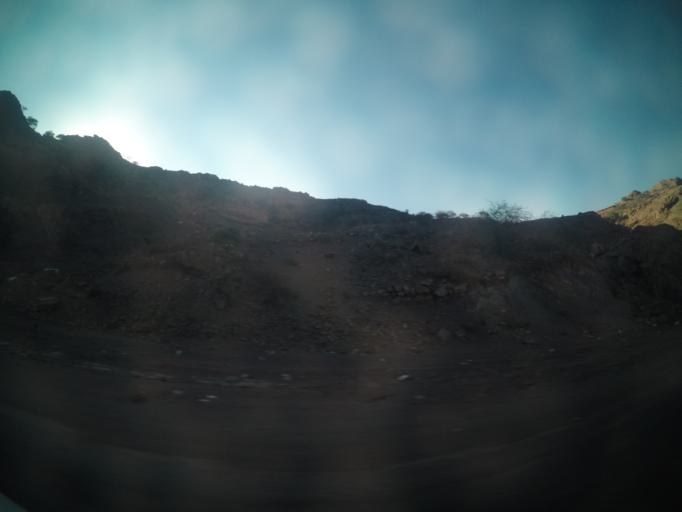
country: YE
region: Ad Dali'
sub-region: Ad Dhale'e
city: Dhalie
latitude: 13.6710
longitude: 44.7669
